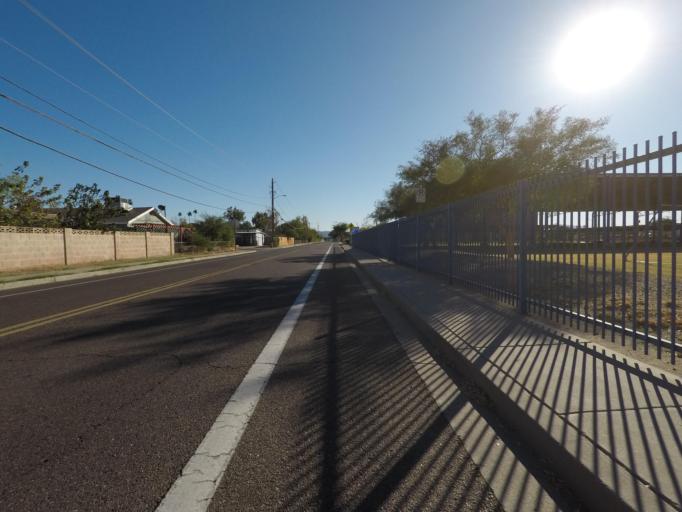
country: US
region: Arizona
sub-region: Maricopa County
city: Phoenix
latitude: 33.4783
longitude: -112.1085
